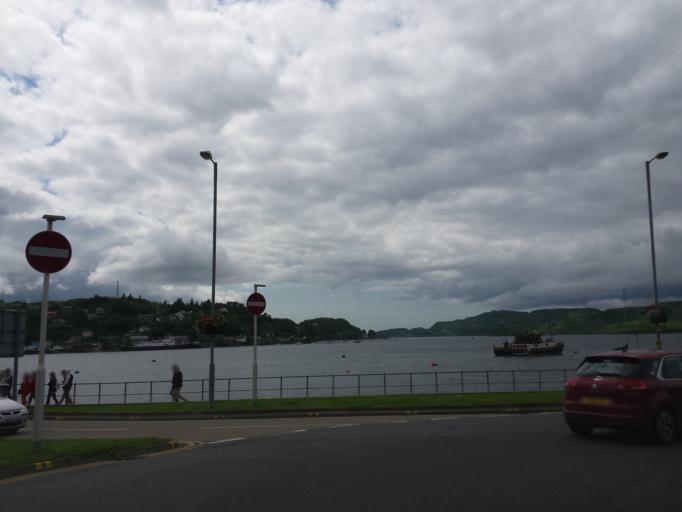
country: GB
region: Scotland
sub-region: Argyll and Bute
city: Oban
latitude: 56.4183
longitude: -5.4755
